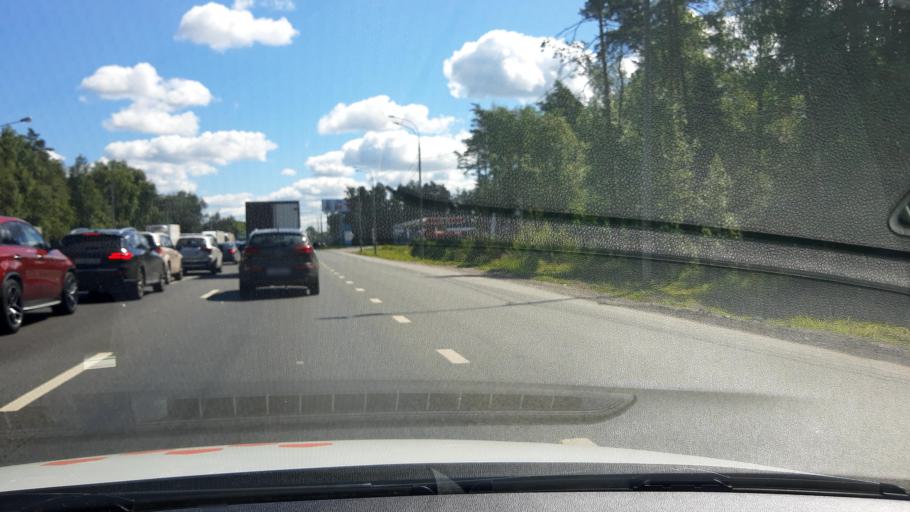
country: RU
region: Moskovskaya
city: Zarya
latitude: 55.8117
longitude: 38.0995
